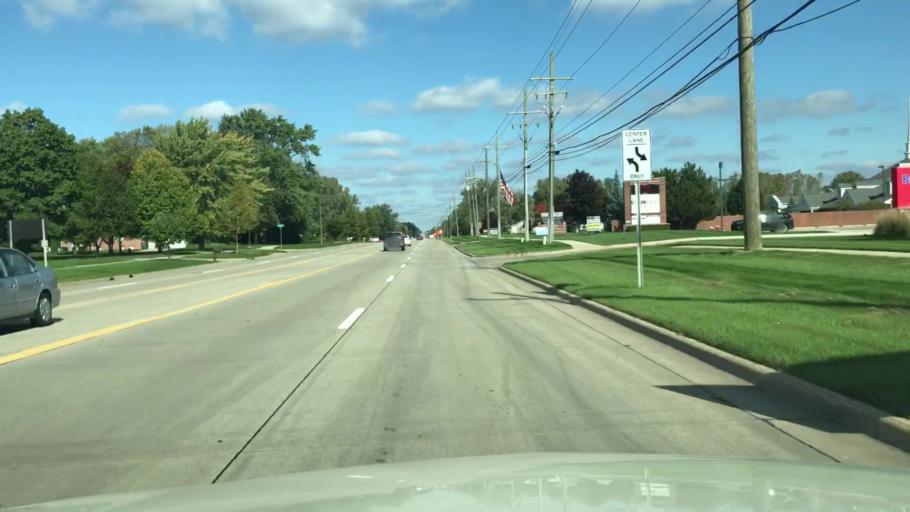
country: US
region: Michigan
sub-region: Macomb County
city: Sterling Heights
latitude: 42.5792
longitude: -83.0893
